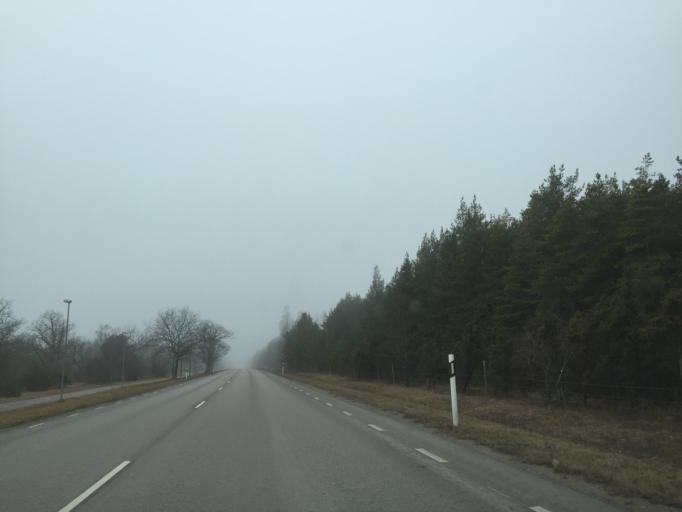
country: EE
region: Saare
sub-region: Kuressaare linn
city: Kuressaare
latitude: 58.2389
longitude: 22.4396
